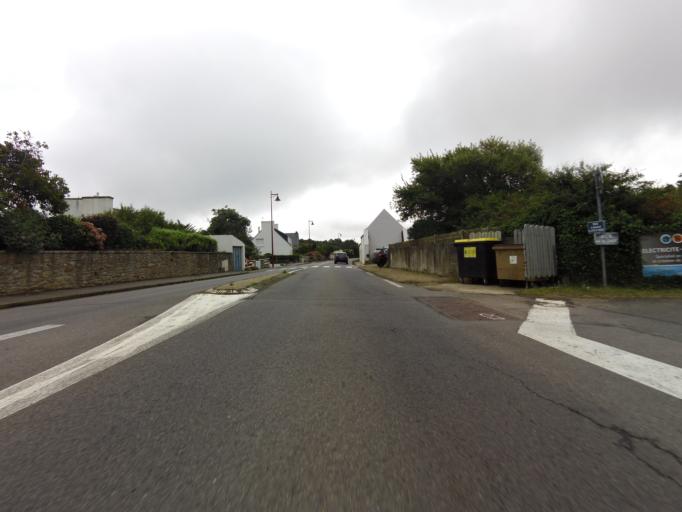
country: FR
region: Brittany
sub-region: Departement du Finistere
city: Plouhinec
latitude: 48.0127
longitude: -4.4768
